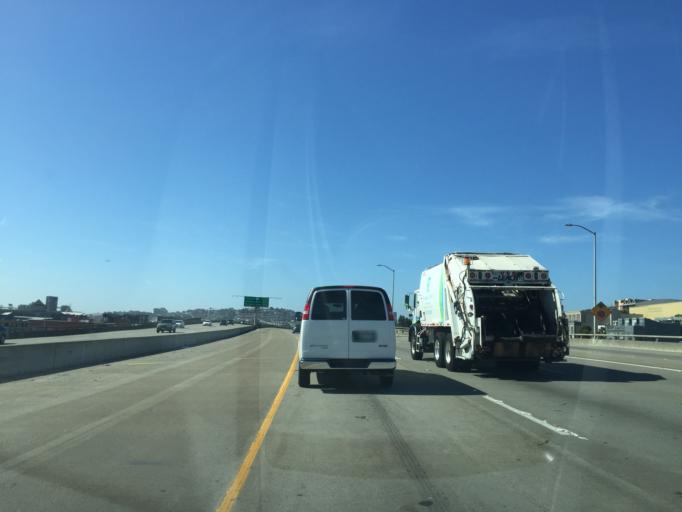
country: US
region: California
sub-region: San Francisco County
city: San Francisco
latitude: 37.7558
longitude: -122.3922
